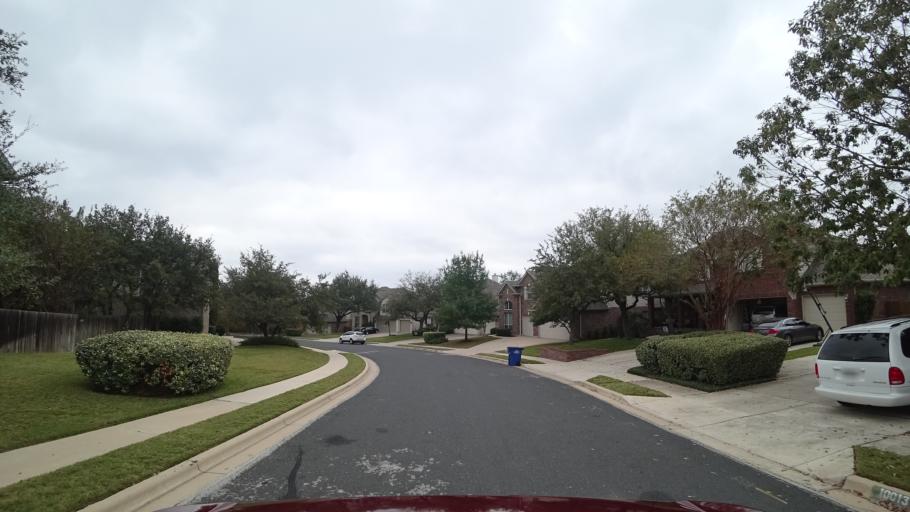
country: US
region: Texas
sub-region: Williamson County
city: Anderson Mill
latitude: 30.4342
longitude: -97.8249
